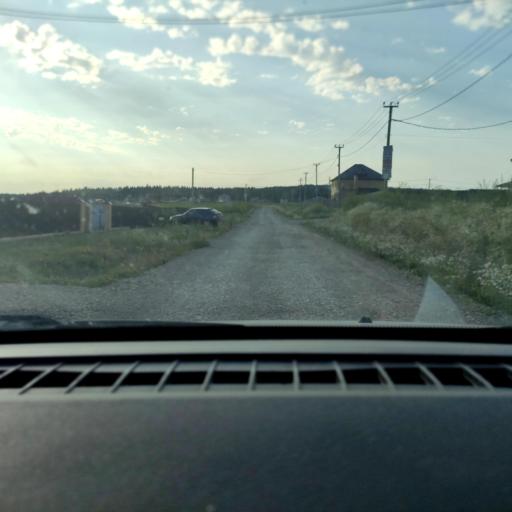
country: RU
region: Perm
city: Ferma
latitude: 57.9499
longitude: 56.3577
